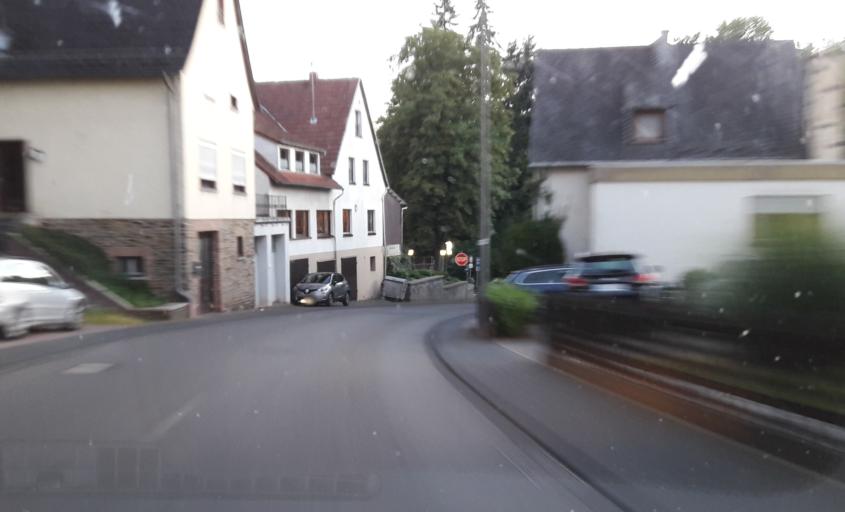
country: DE
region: Rheinland-Pfalz
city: Urzig
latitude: 49.9829
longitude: 7.0040
